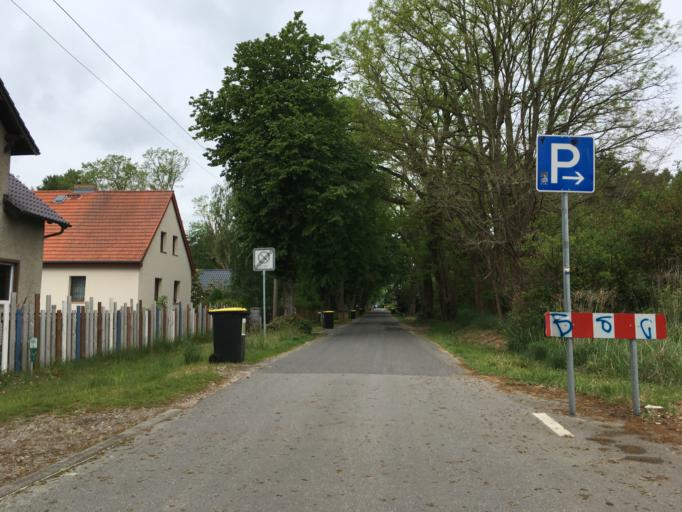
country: DE
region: Brandenburg
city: Wandlitz
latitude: 52.7517
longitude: 13.4808
